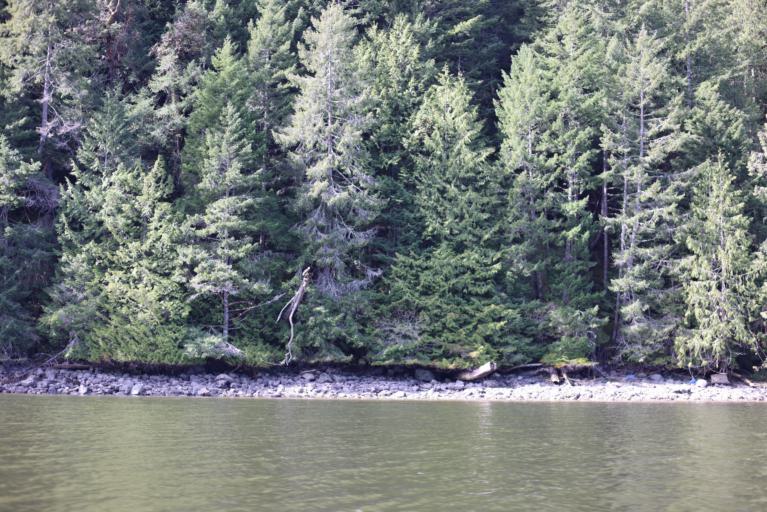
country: CA
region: British Columbia
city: Langford
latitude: 48.5310
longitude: -123.5488
